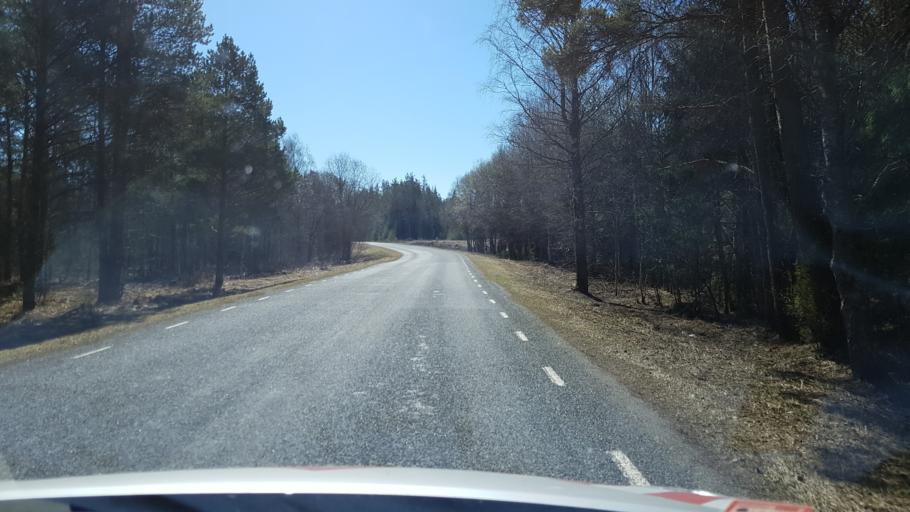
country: EE
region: Laeaene-Virumaa
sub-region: Haljala vald
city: Haljala
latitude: 59.5008
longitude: 26.2396
